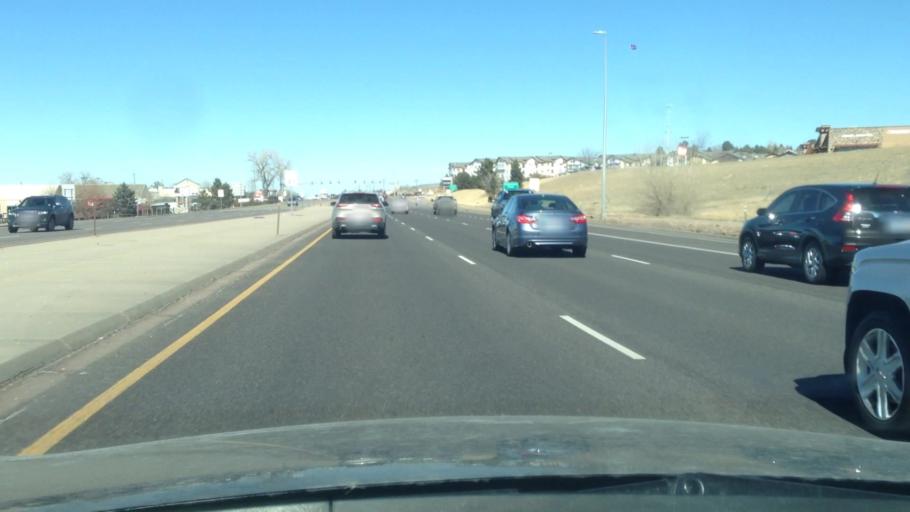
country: US
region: Colorado
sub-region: Douglas County
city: Stonegate
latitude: 39.5552
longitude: -104.7781
